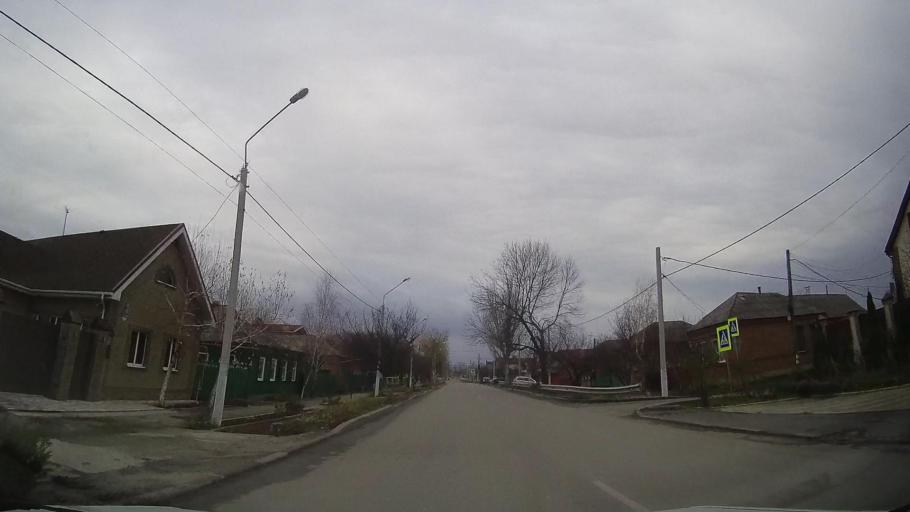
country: RU
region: Rostov
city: Bataysk
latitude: 47.1192
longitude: 39.7436
